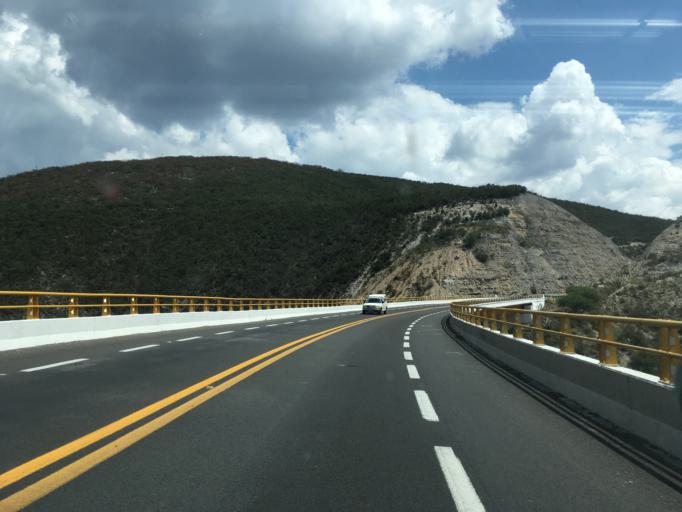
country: MX
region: Puebla
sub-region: San Jose Miahuatlan
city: San Pedro Tetitlan
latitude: 18.0273
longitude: -97.3473
